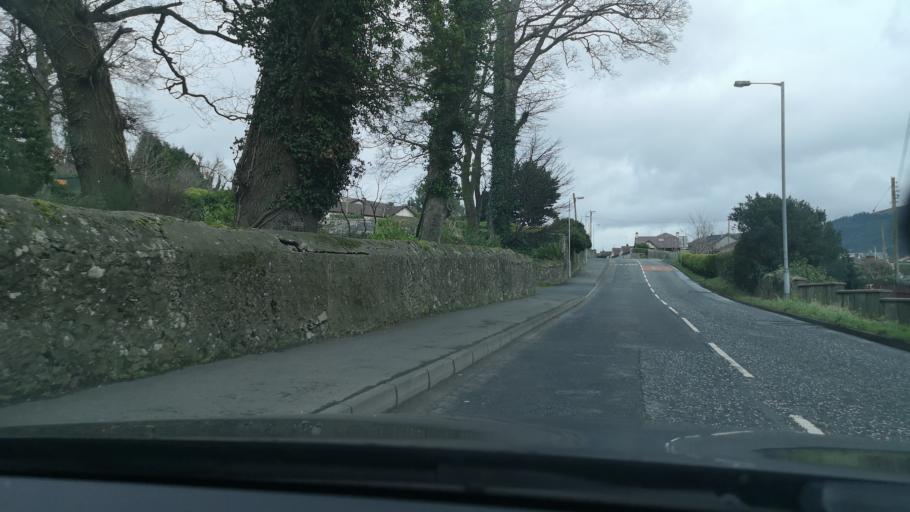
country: GB
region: Northern Ireland
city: Rostrevor
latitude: 54.1052
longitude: -6.1911
